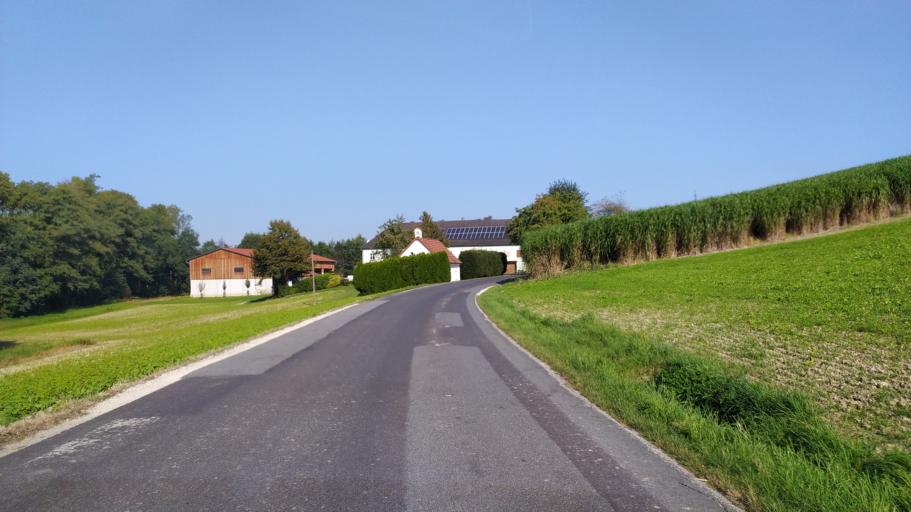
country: AT
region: Lower Austria
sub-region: Politischer Bezirk Amstetten
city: Zeillern
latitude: 48.1085
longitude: 14.7504
